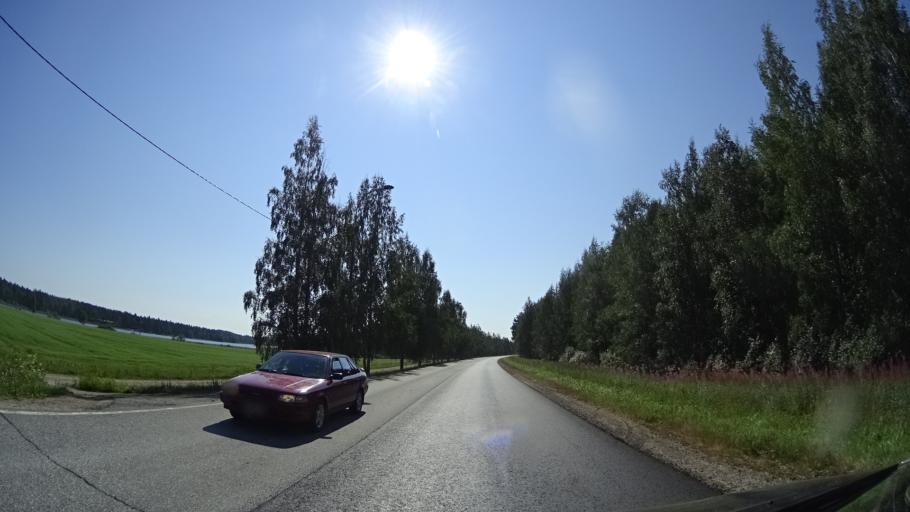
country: FI
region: North Karelia
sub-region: Joensuu
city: Juuka
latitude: 63.2448
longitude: 29.2724
